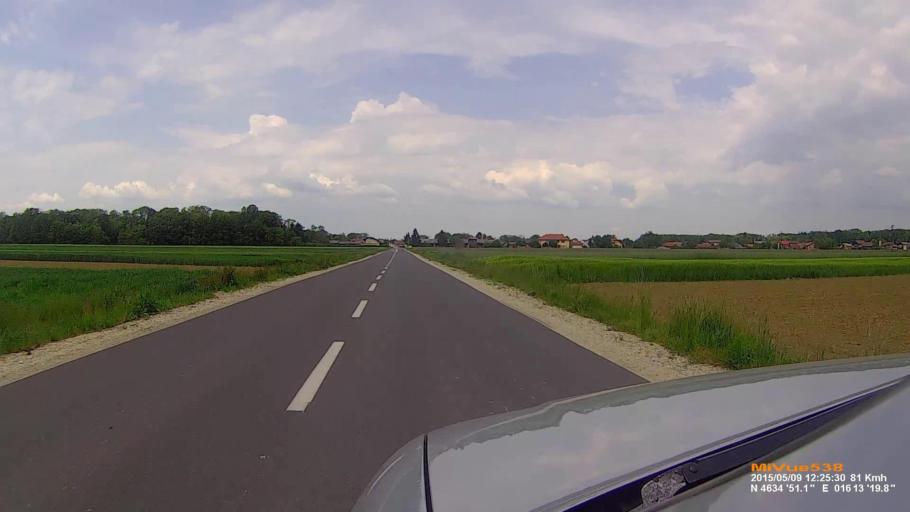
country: SI
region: Beltinci
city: Beltinci
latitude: 46.5810
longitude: 16.2220
